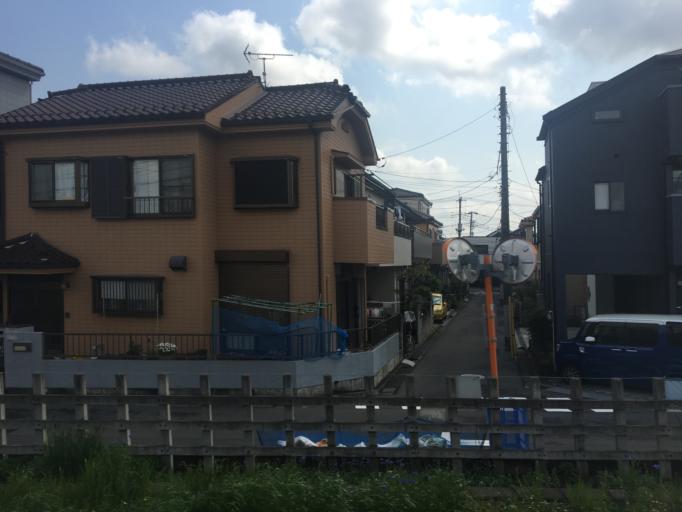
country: JP
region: Saitama
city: Kamifukuoka
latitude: 35.8649
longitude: 139.5196
